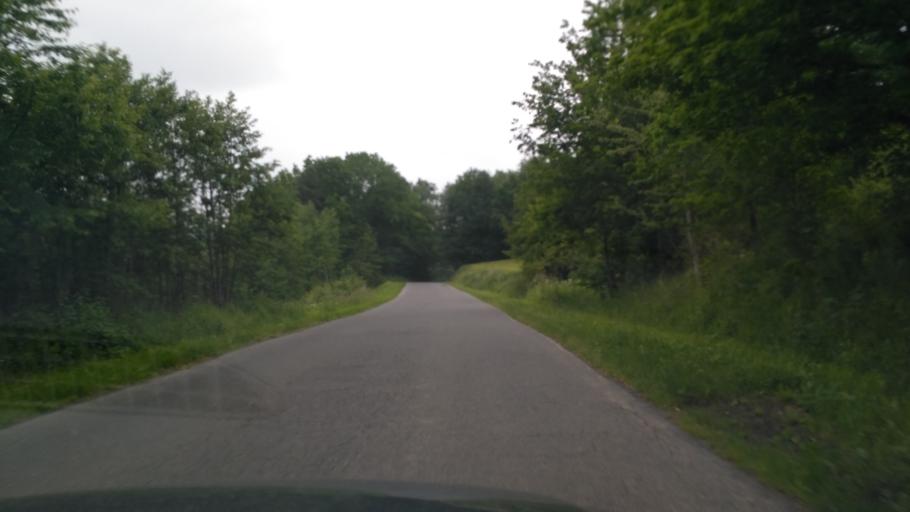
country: PL
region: Subcarpathian Voivodeship
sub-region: Powiat ropczycko-sedziszowski
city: Zagorzyce
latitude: 50.0103
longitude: 21.6771
